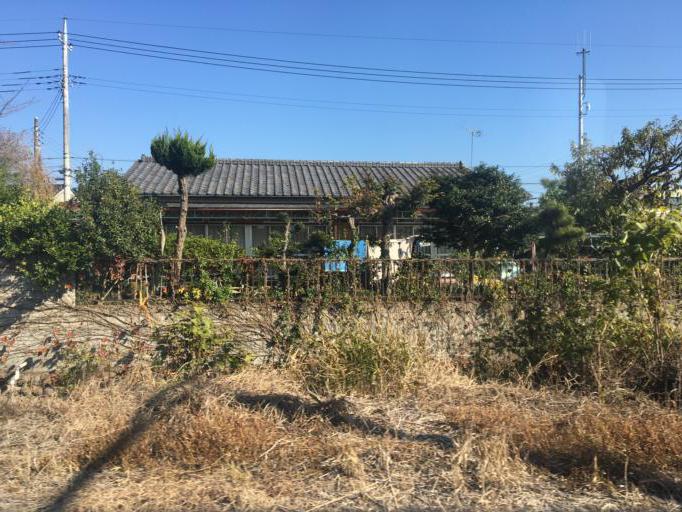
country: JP
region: Gunma
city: Kiryu
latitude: 36.3732
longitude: 139.3769
